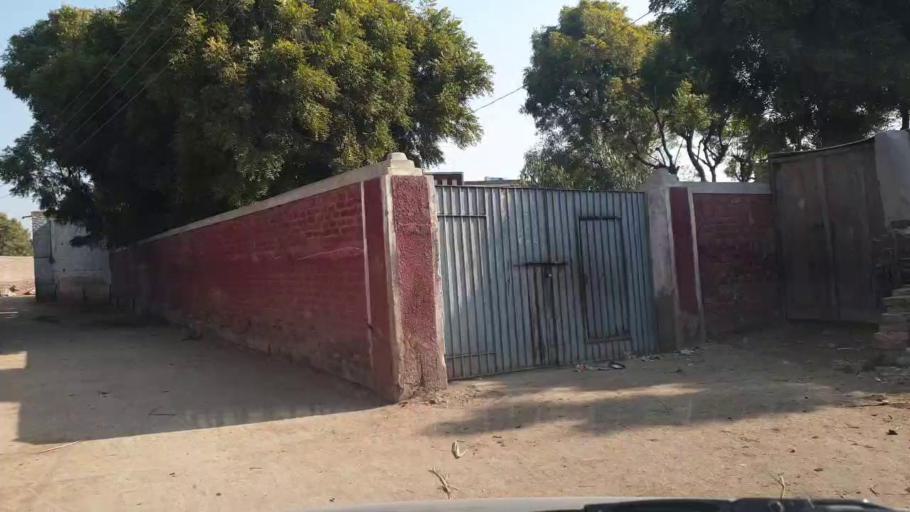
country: PK
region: Sindh
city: Tando Allahyar
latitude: 25.4268
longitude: 68.7568
